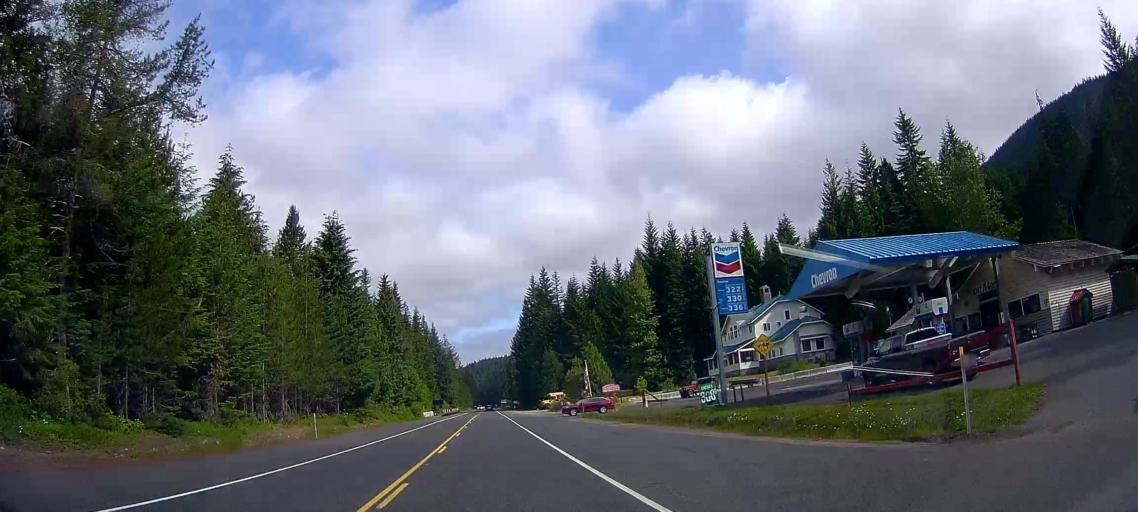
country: US
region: Oregon
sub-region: Clackamas County
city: Mount Hood Village
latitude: 45.2518
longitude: -121.7108
